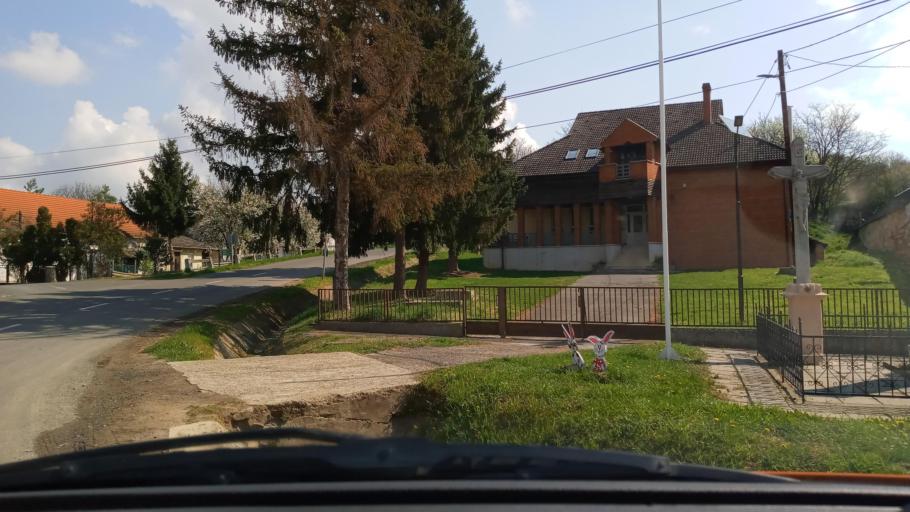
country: HU
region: Baranya
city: Pecsvarad
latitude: 46.1006
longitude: 18.4594
